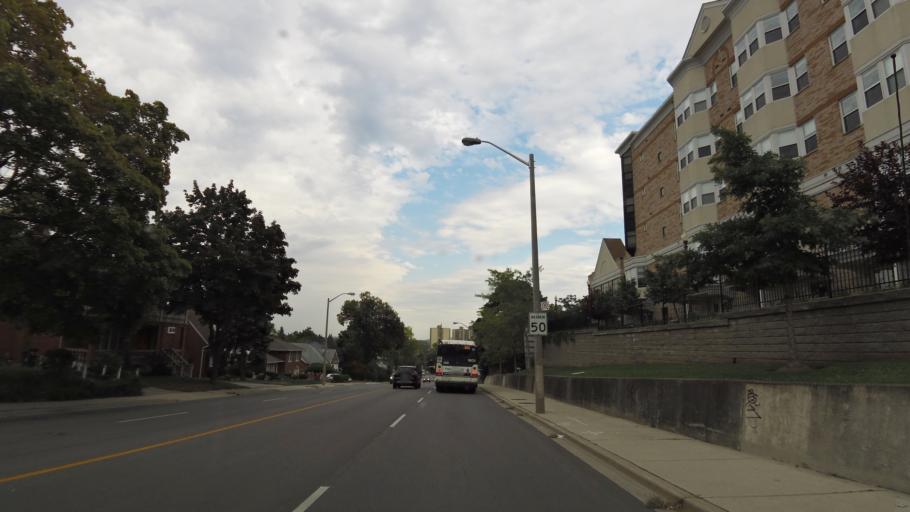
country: CA
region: Ontario
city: Etobicoke
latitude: 43.6975
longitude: -79.5263
